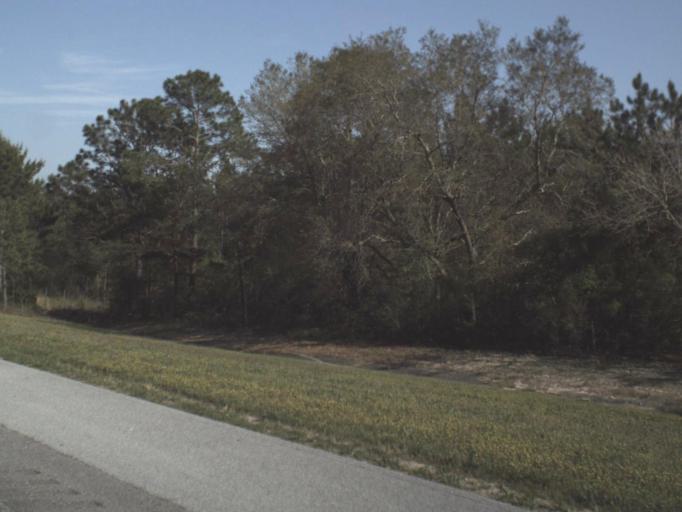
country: US
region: Florida
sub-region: Okaloosa County
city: Crestview
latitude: 30.7172
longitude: -86.4446
